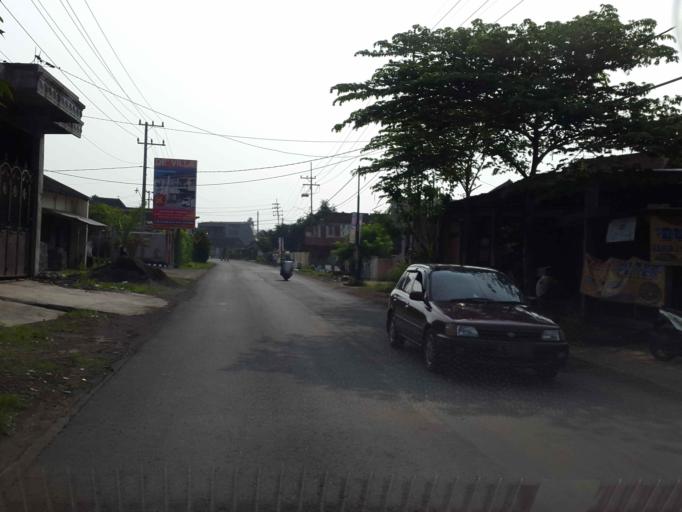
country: ID
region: East Java
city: Kambingan
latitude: -7.9678
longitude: 112.6868
